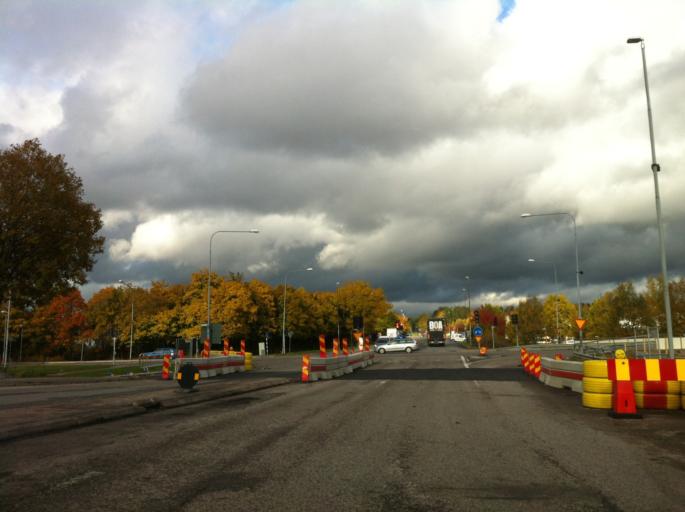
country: SE
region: Stockholm
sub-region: Upplands Vasby Kommun
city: Upplands Vaesby
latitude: 59.5139
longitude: 17.9189
